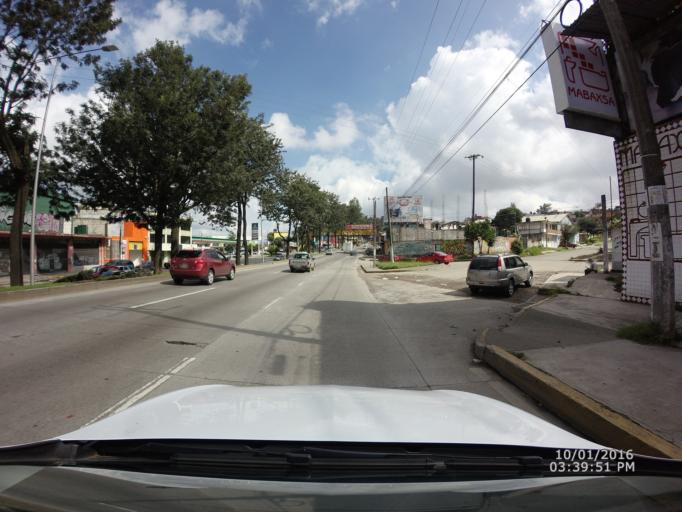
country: MX
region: Veracruz
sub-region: Xalapa
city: Xalapa de Enriquez
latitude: 19.5573
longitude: -96.9163
